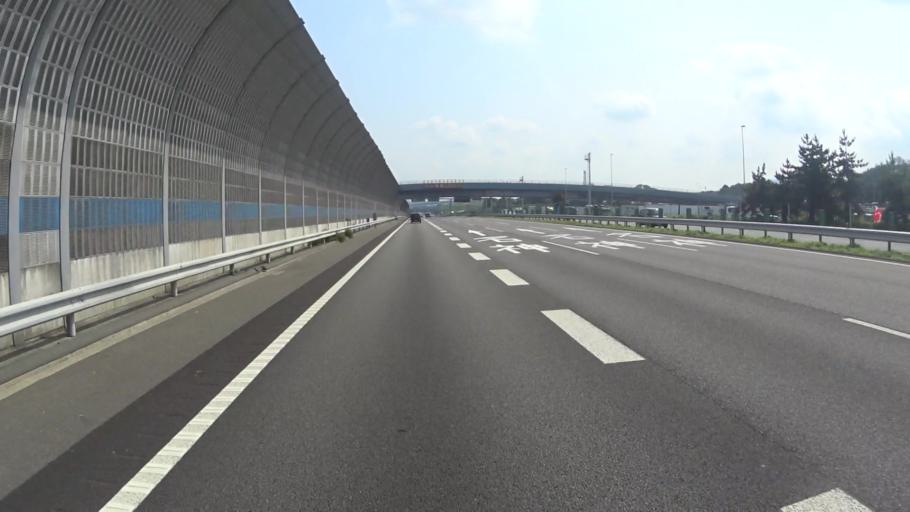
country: JP
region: Shiga Prefecture
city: Kusatsu
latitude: 34.9775
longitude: 135.9481
